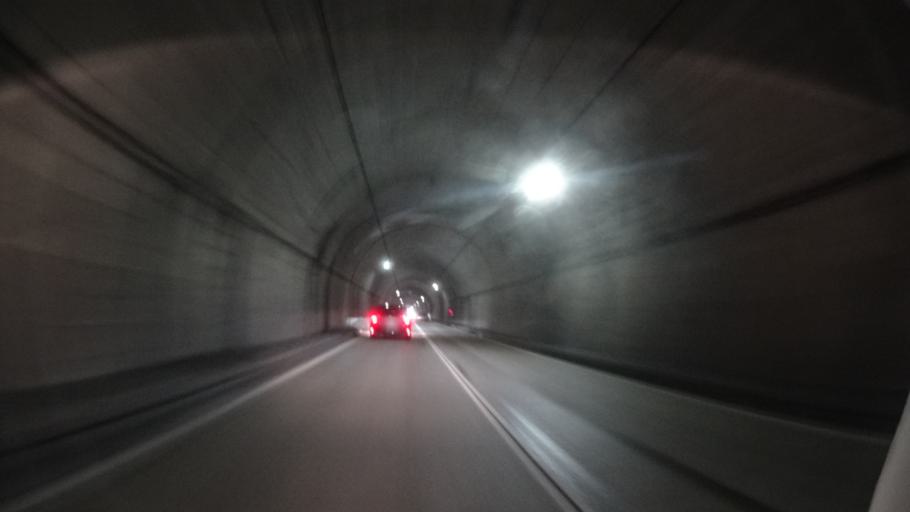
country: JP
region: Fukui
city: Ono
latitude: 35.9593
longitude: 136.6093
